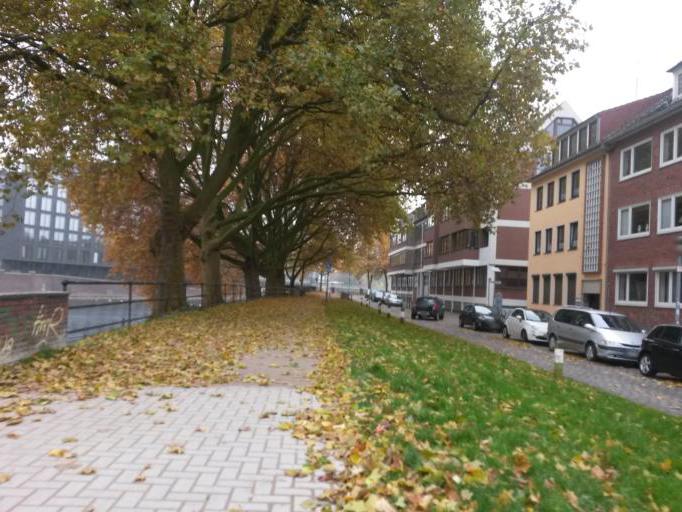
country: DE
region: Bremen
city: Bremen
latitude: 53.0744
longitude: 8.8001
